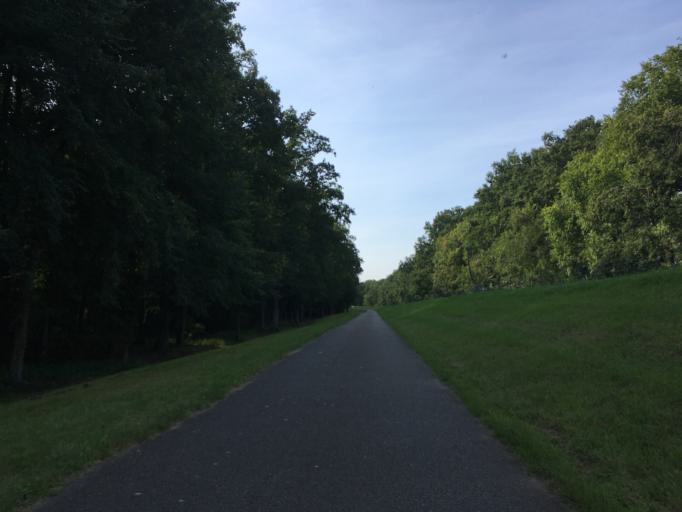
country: DE
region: Brandenburg
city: Wiesenau
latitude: 52.2672
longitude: 14.6241
